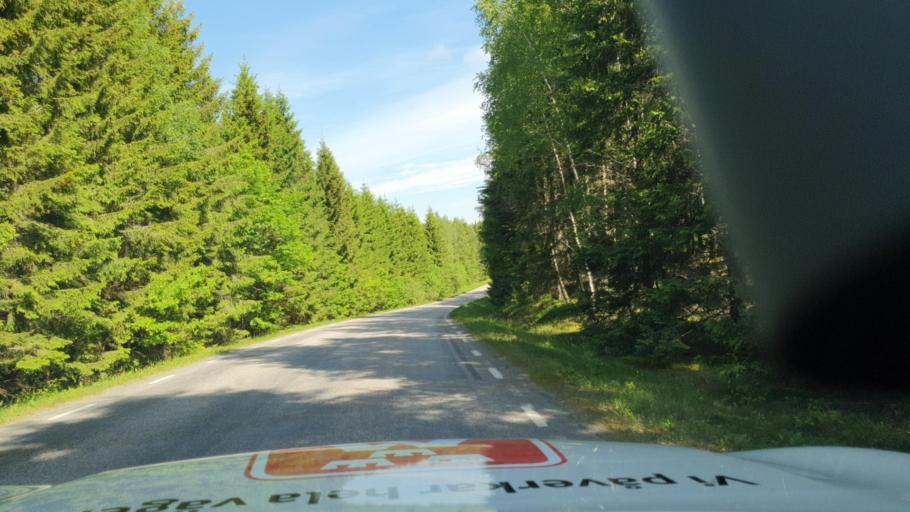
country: SE
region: Vaestra Goetaland
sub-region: Herrljunga Kommun
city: Herrljunga
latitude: 58.0886
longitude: 13.1097
